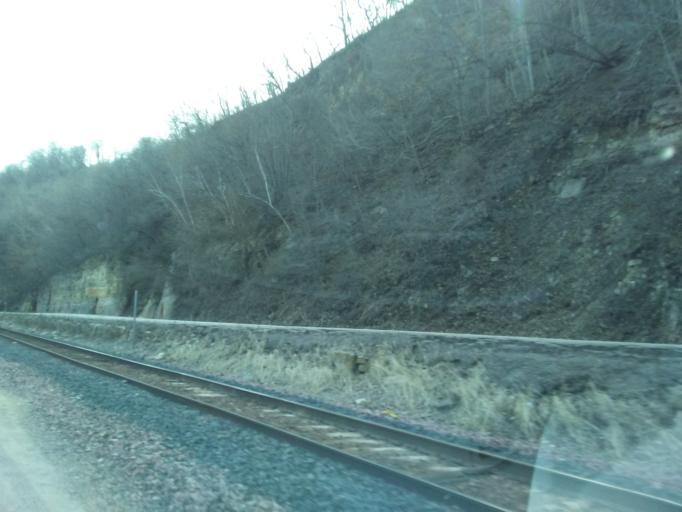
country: US
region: Wisconsin
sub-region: Crawford County
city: Prairie du Chien
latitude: 43.0671
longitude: -91.1803
